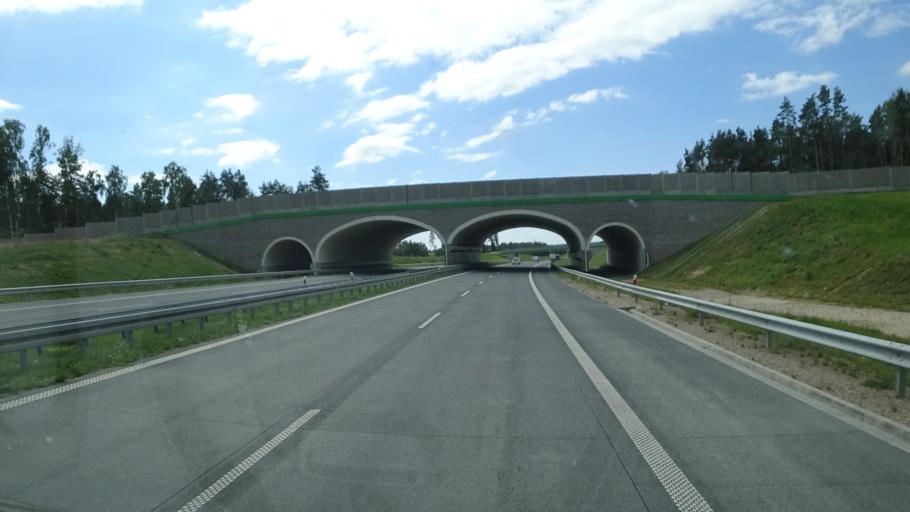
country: PL
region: Podlasie
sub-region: Powiat grajewski
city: Szczuczyn
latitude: 53.5177
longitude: 22.2567
